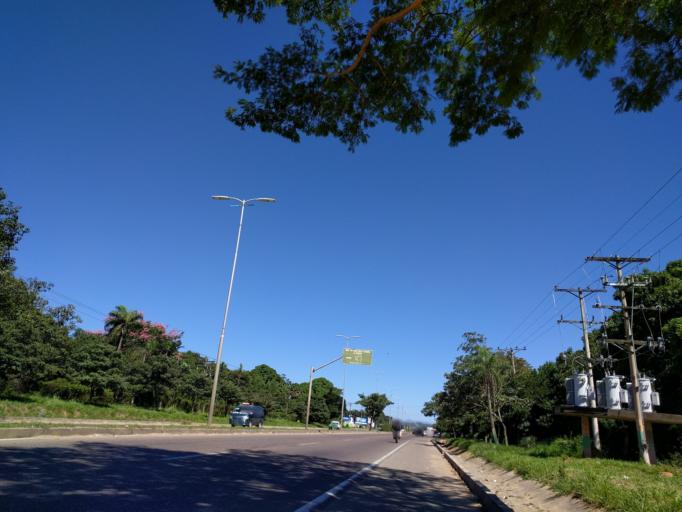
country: BO
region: Santa Cruz
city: Santa Cruz de la Sierra
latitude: -17.8685
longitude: -63.2725
